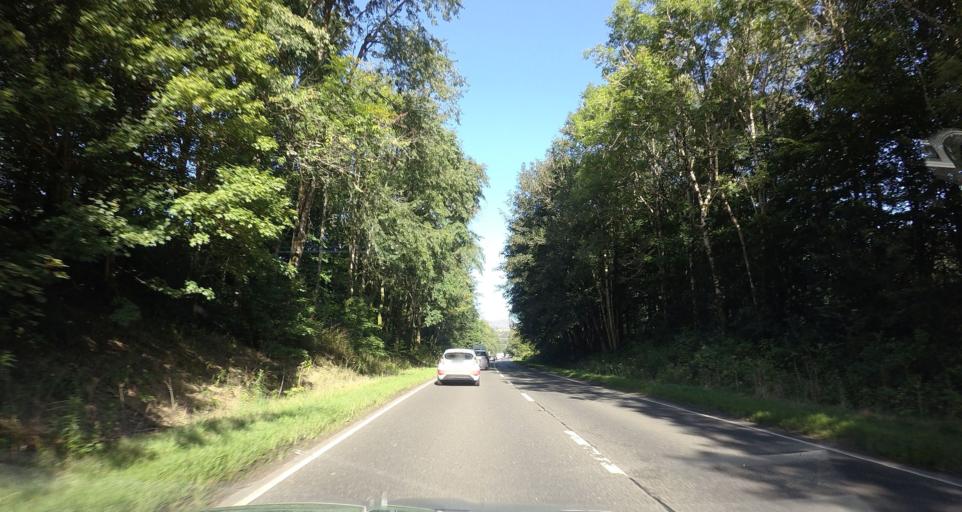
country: GB
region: Scotland
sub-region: Stirling
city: Callander
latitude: 56.2283
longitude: -4.1741
